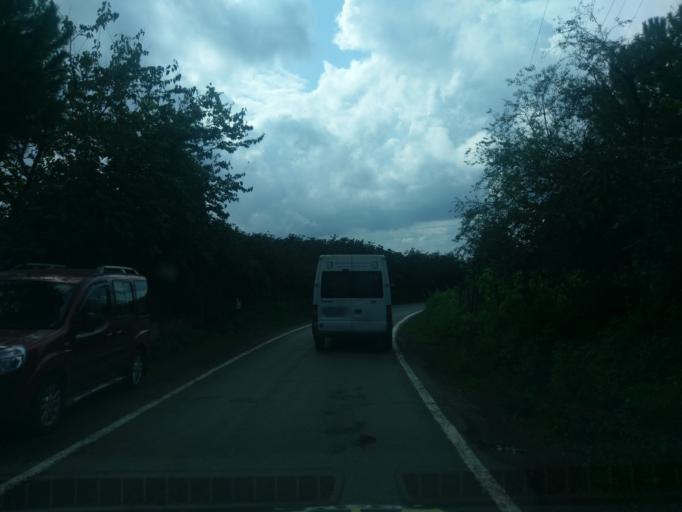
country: TR
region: Ordu
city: Camas
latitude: 40.9107
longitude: 37.6122
